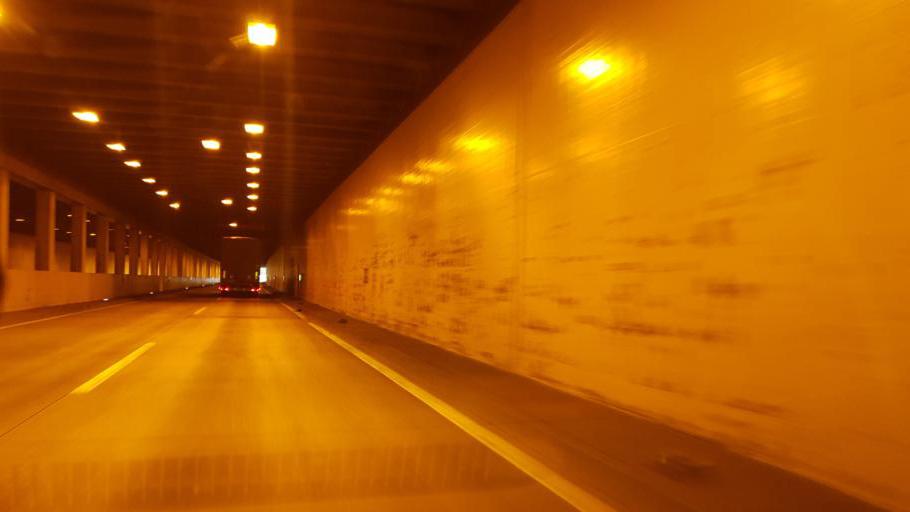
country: AT
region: Carinthia
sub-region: Villach Stadt
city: Villach
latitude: 46.6401
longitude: 13.8888
